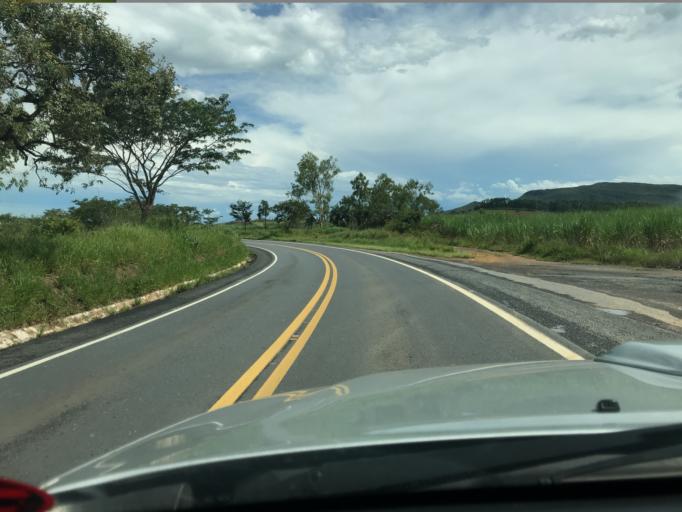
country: BR
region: Minas Gerais
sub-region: Campos Altos
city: Campos Altos
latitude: -19.8095
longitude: -46.0329
